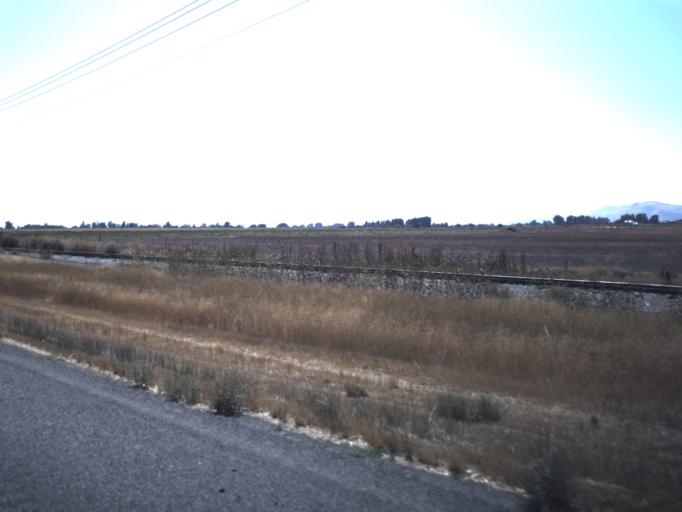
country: US
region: Utah
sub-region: Cache County
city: Lewiston
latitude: 41.9738
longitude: -111.8130
